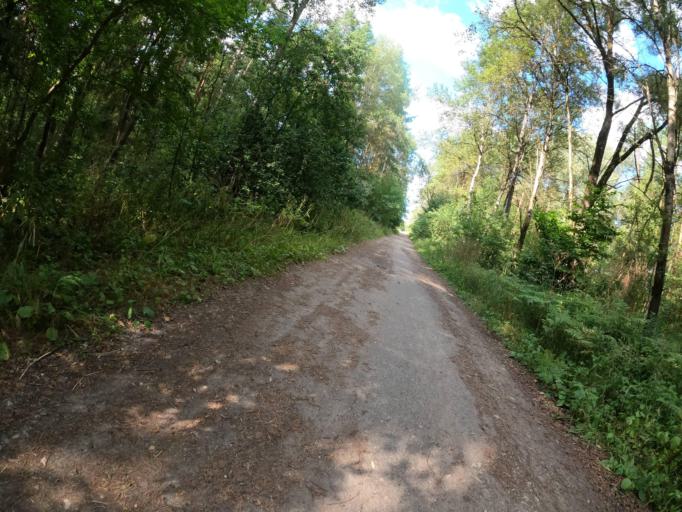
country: RU
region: Moskovskaya
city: Lopatinskiy
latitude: 55.3853
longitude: 38.7088
